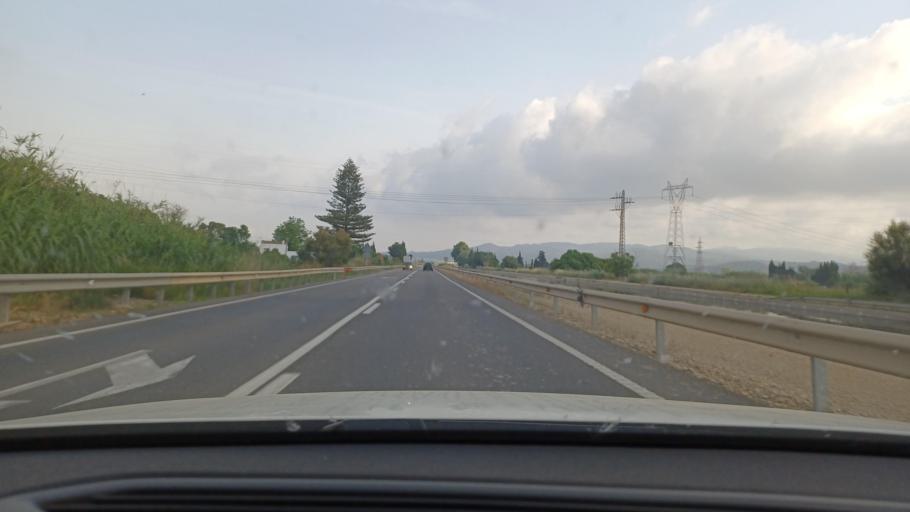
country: ES
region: Catalonia
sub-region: Provincia de Tarragona
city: Amposta
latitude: 40.7287
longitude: 0.5708
